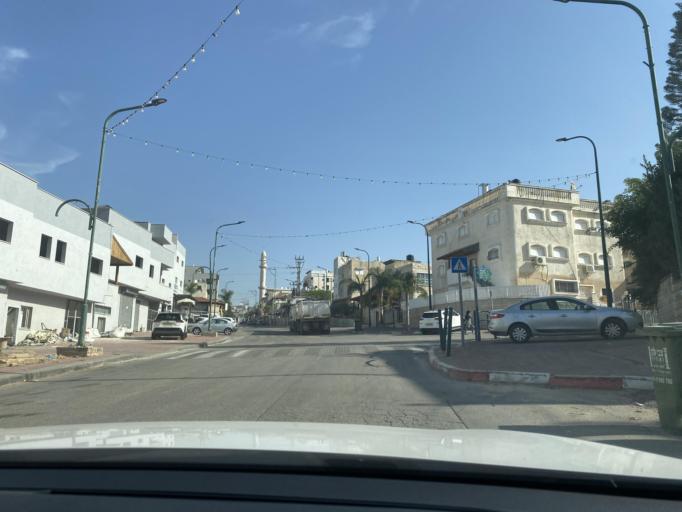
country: IL
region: Central District
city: Kafr Qasim
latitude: 32.1315
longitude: 34.9665
